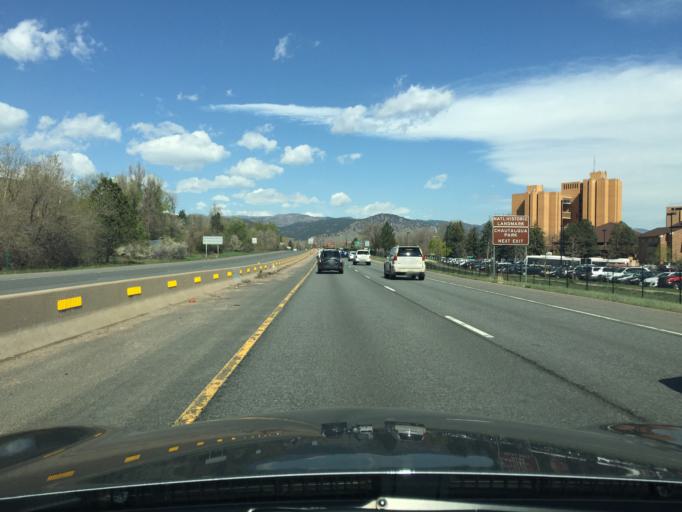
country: US
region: Colorado
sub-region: Boulder County
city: Boulder
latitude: 39.9954
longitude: -105.2502
